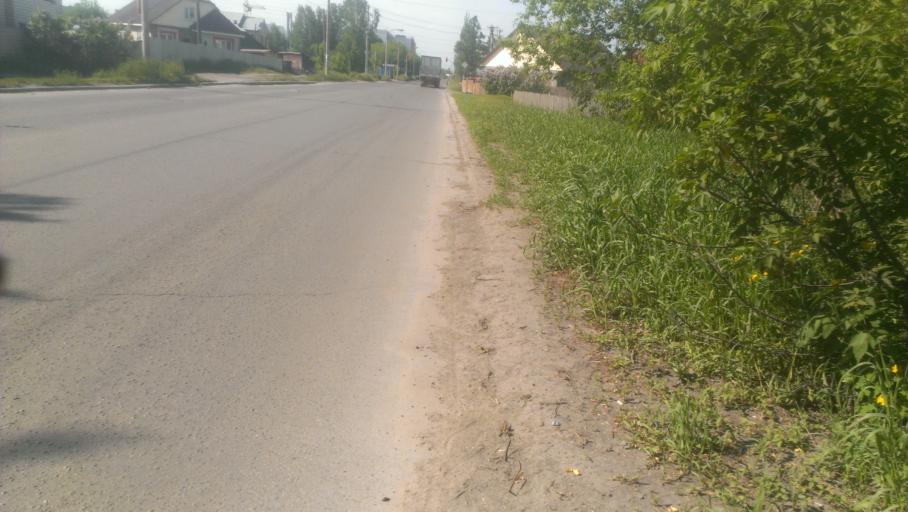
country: RU
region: Altai Krai
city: Novoaltaysk
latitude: 53.4055
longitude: 83.9449
